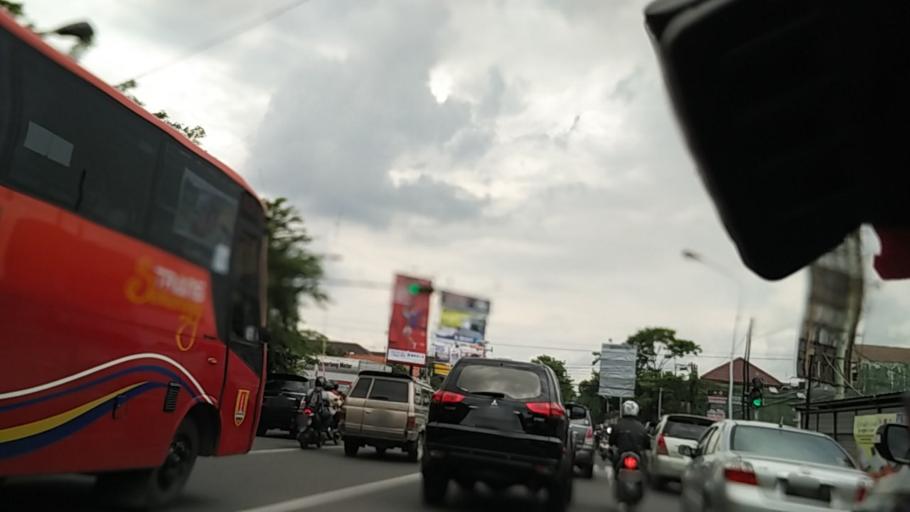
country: ID
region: Central Java
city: Semarang
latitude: -6.9944
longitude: 110.4339
